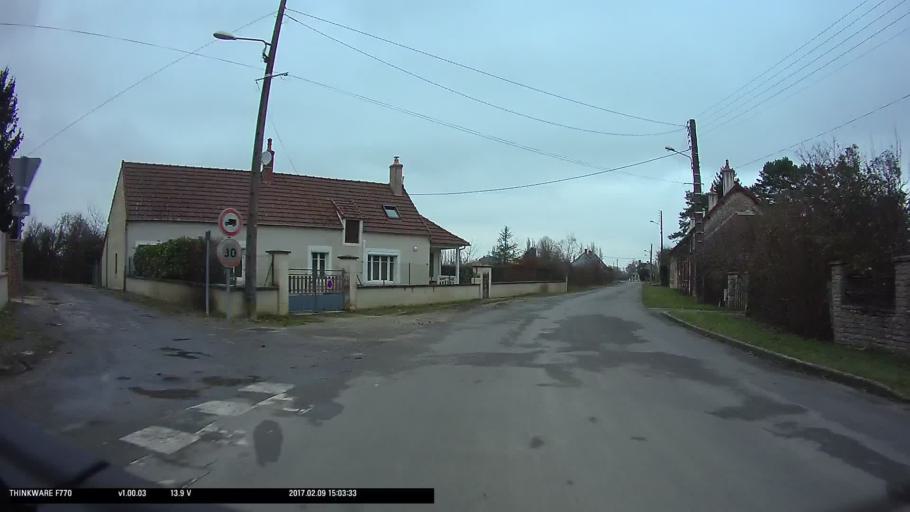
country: FR
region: Centre
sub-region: Departement du Cher
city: Orval
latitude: 46.8074
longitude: 2.4614
